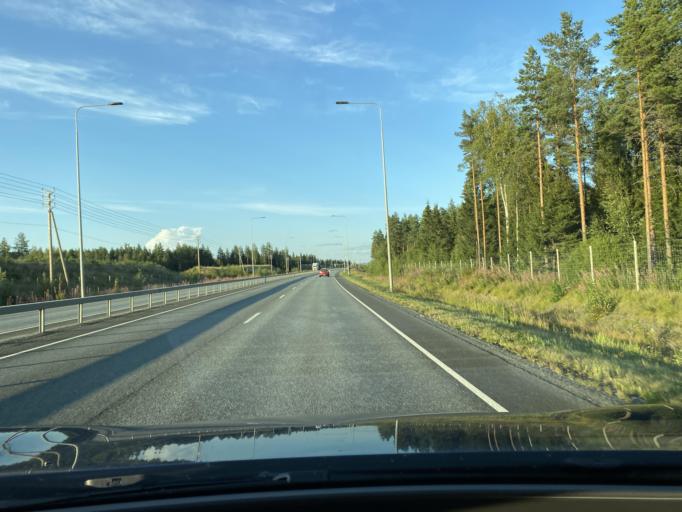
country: FI
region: Southern Ostrobothnia
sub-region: Seinaejoki
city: Seinaejoki
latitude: 62.7316
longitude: 22.8939
